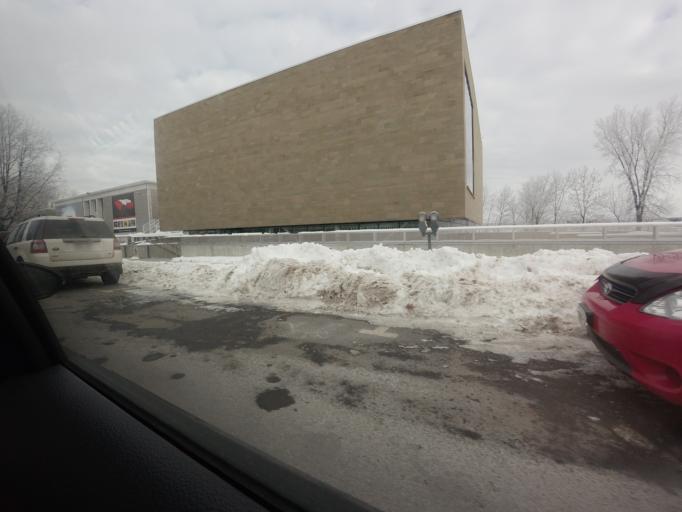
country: CA
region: New Brunswick
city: Fredericton
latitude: 45.9594
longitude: -66.6353
